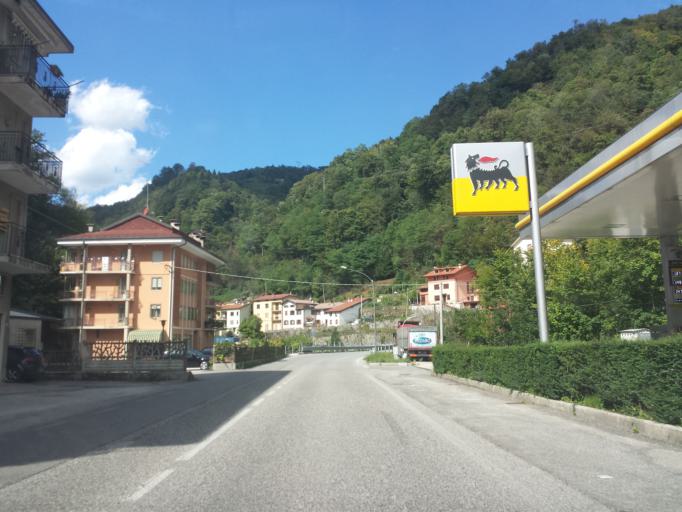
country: IT
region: Veneto
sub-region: Provincia di Vicenza
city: Recoaro Terme
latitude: 45.7049
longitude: 11.2407
